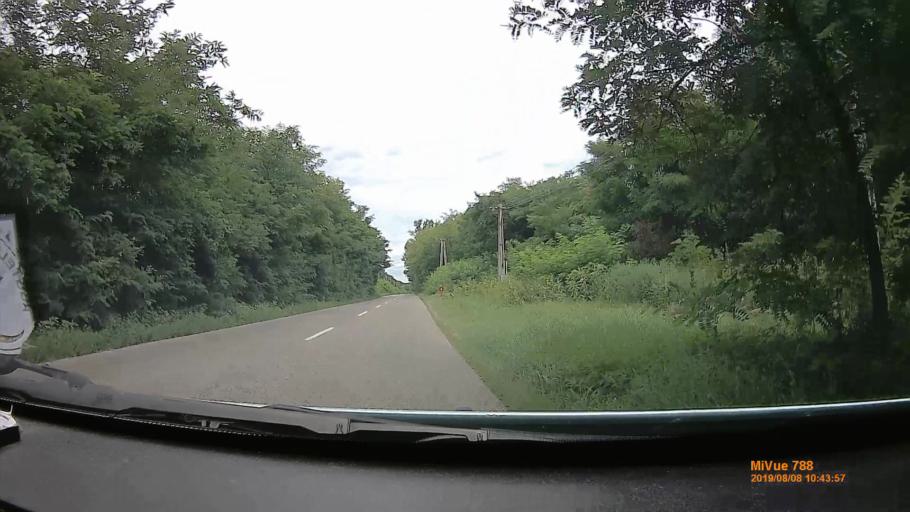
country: HU
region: Szabolcs-Szatmar-Bereg
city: Balkany
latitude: 47.7256
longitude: 21.8747
